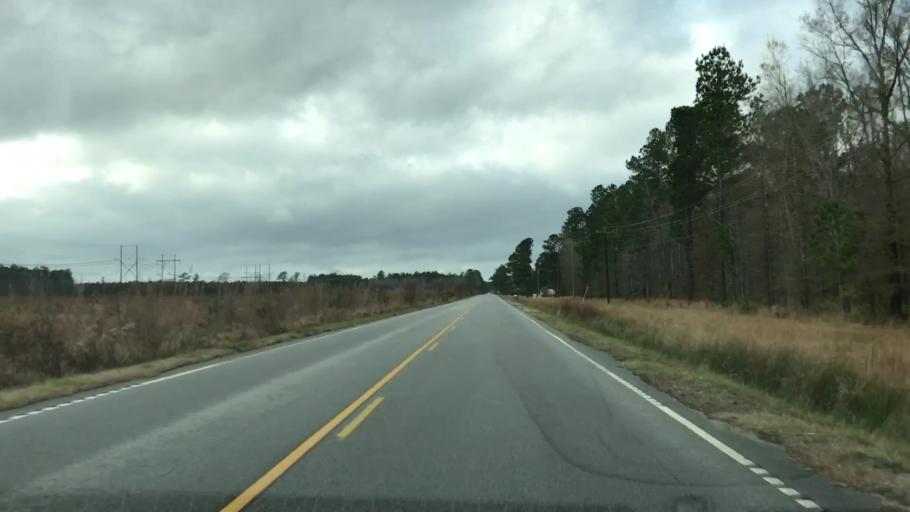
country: US
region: South Carolina
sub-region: Berkeley County
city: Saint Stephen
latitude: 33.2820
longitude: -79.7338
